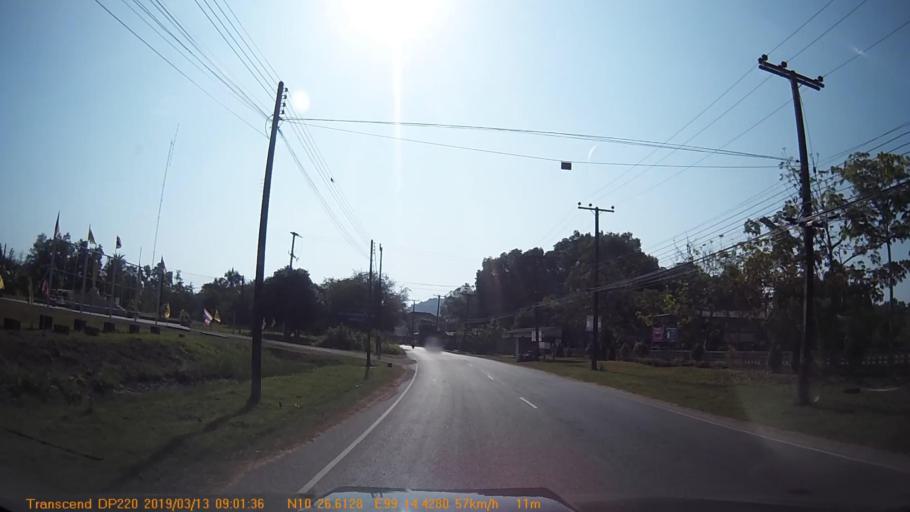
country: TH
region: Chumphon
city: Chumphon
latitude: 10.4435
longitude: 99.2406
